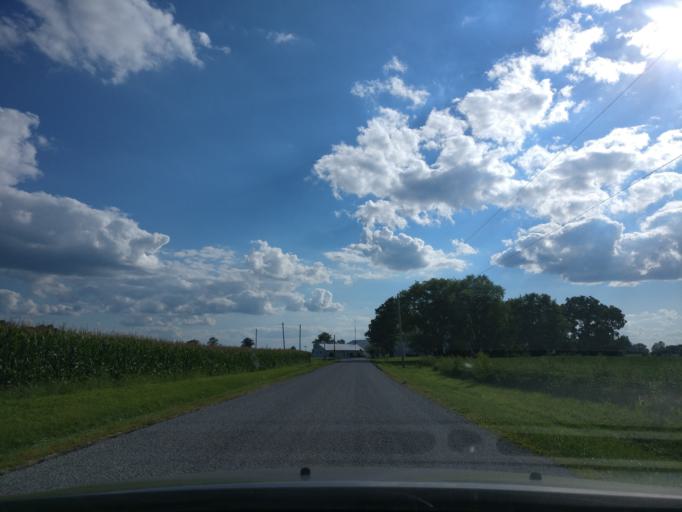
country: US
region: Ohio
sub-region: Clinton County
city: Wilmington
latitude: 39.5173
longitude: -83.7821
